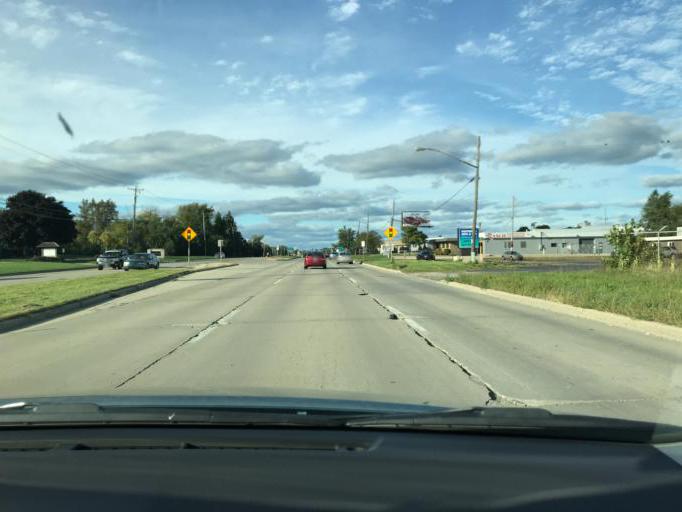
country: US
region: Wisconsin
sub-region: Kenosha County
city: Somers
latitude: 42.5924
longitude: -87.8813
